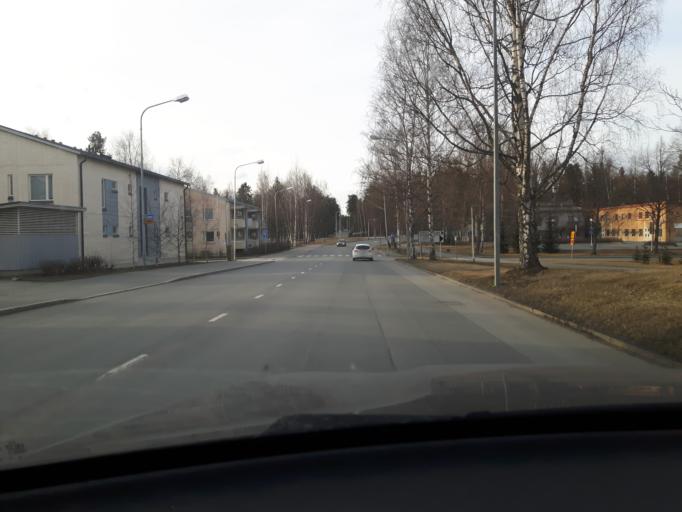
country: FI
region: Pirkanmaa
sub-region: Etelae-Pirkanmaa
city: Valkeakoski
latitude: 61.2698
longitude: 24.0297
